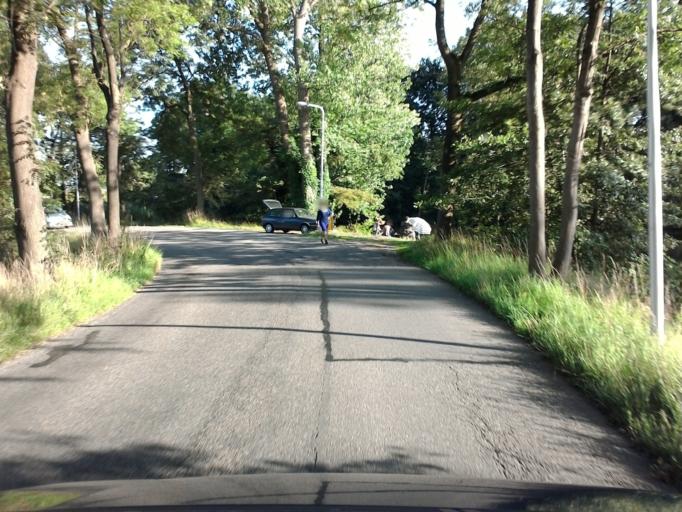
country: NL
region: Utrecht
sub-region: Gemeente Utrecht
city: Utrecht
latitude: 52.1176
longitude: 5.1405
